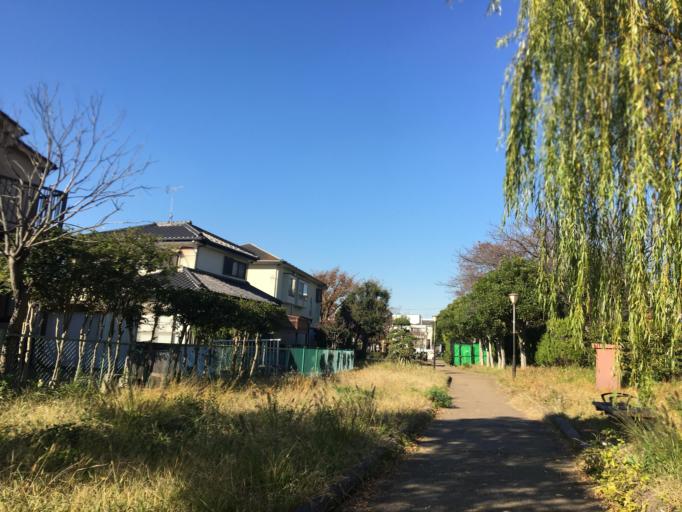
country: JP
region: Tokyo
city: Urayasu
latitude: 35.6887
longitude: 139.9094
